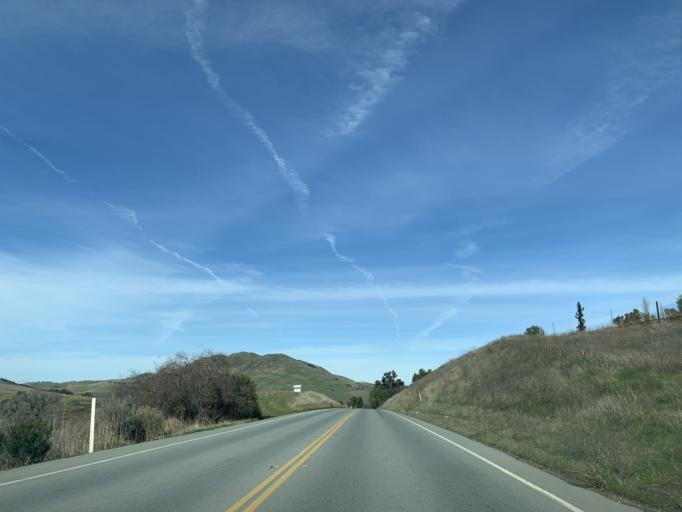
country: US
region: California
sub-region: San Benito County
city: Ridgemark
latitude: 36.7169
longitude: -121.2777
